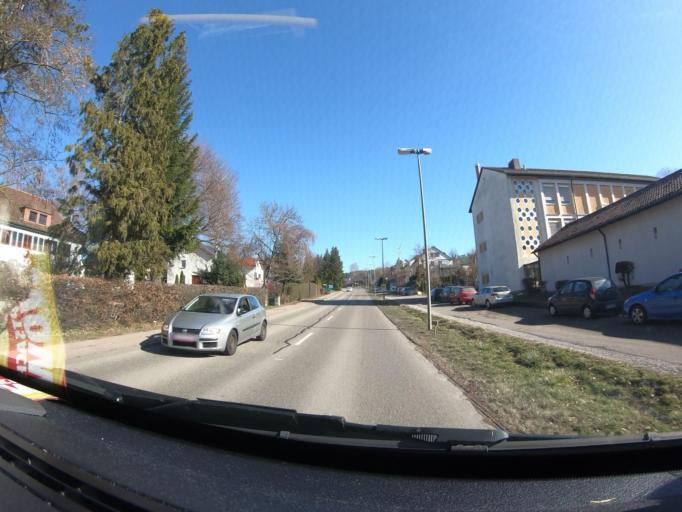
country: DE
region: Baden-Wuerttemberg
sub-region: Regierungsbezirk Stuttgart
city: Gaildorf
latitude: 49.0050
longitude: 9.7751
